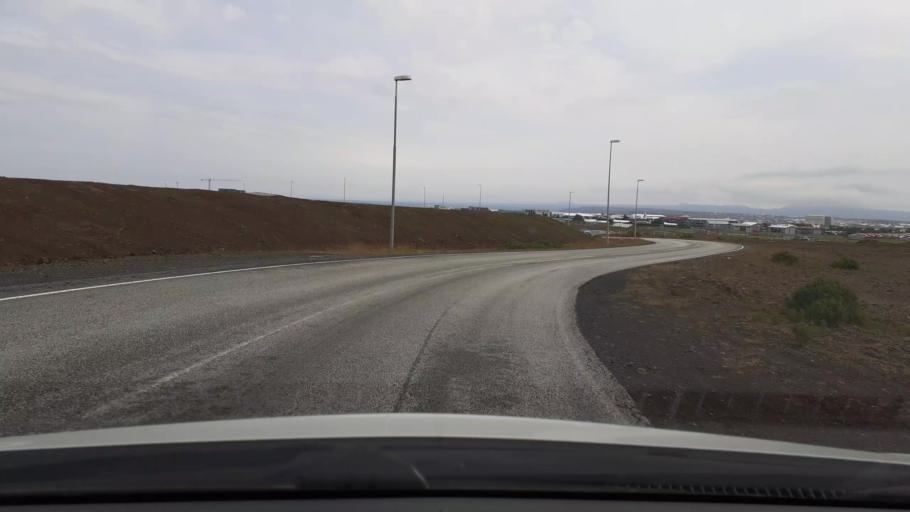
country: IS
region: Southern Peninsula
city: Reykjanesbaer
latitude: 63.9935
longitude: -22.5696
